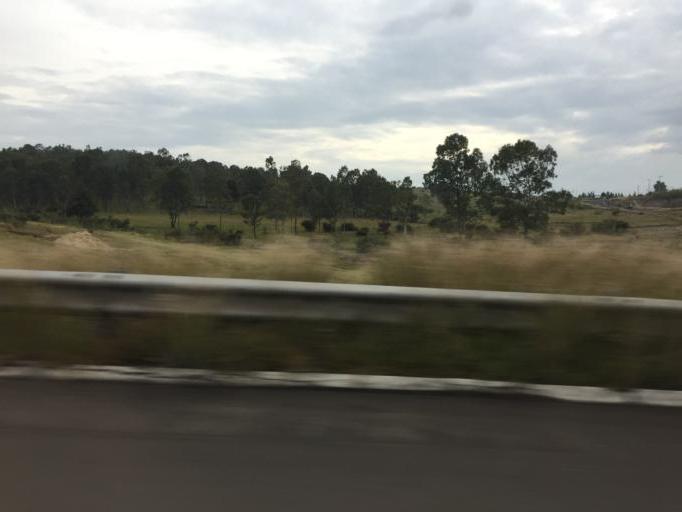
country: MX
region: Mexico
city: Huaniqueo de Morales
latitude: 19.8825
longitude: -101.5097
